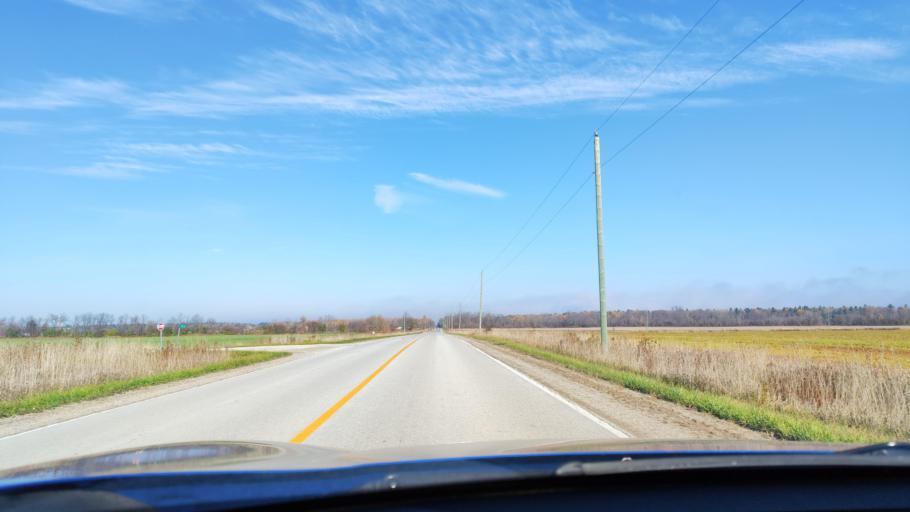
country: CA
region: Ontario
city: Wasaga Beach
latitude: 44.3950
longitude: -80.0567
